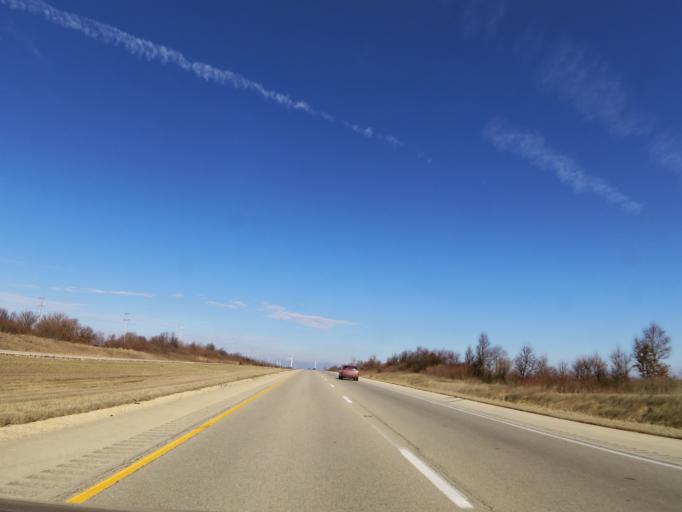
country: US
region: Illinois
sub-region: LaSalle County
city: Mendota
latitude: 41.6372
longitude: -89.0611
